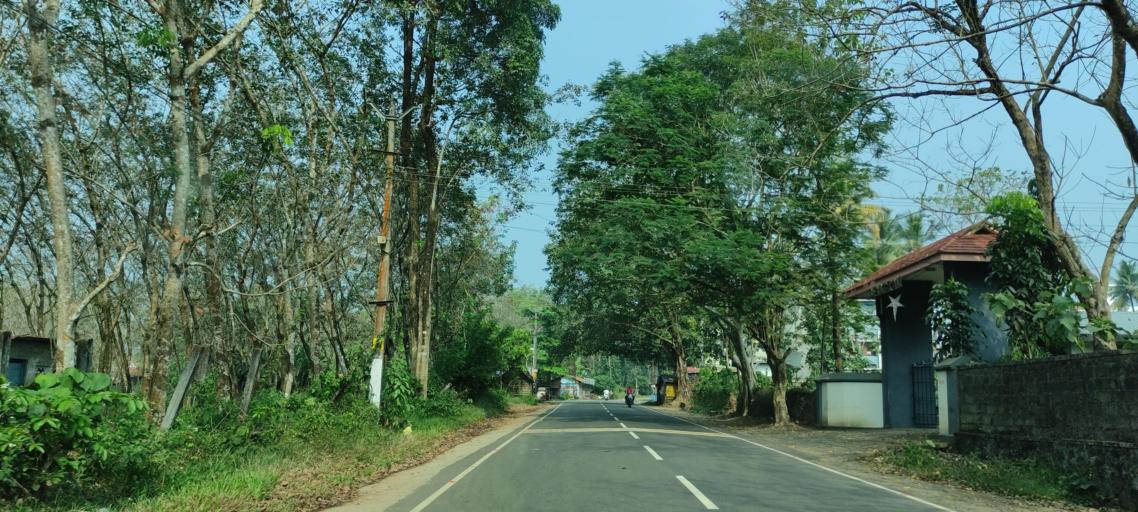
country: IN
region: Kerala
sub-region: Ernakulam
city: Piravam
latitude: 9.7966
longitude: 76.4715
